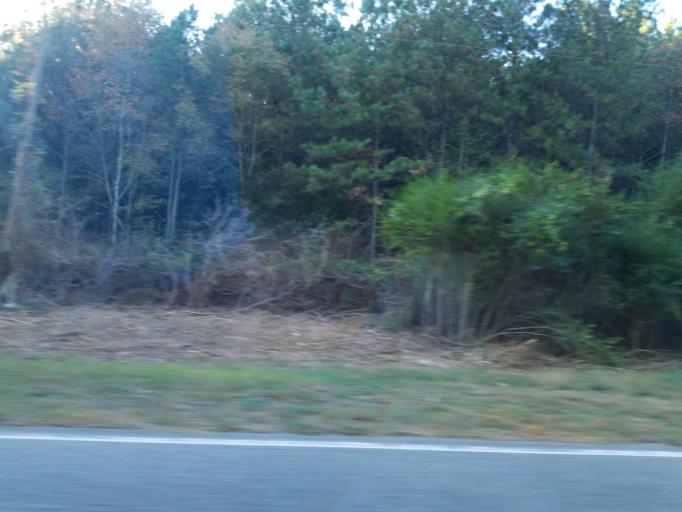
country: US
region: Georgia
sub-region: Bartow County
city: Adairsville
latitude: 34.2952
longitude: -84.9412
